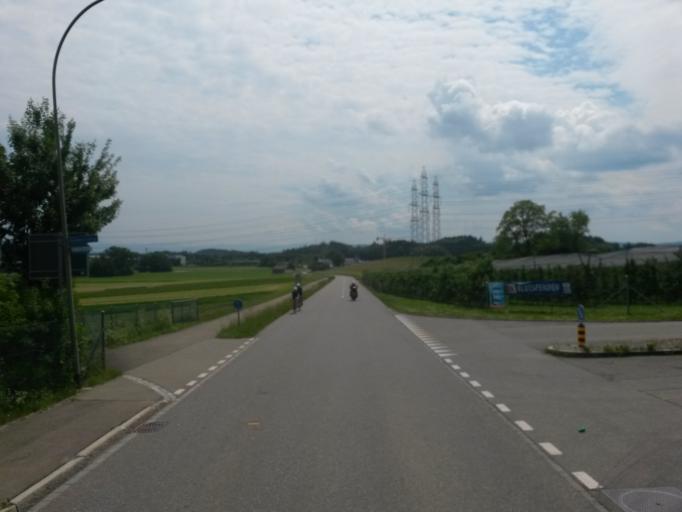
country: CH
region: Zurich
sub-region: Bezirk Pfaeffikon
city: Tagelswangen
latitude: 47.4462
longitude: 8.6818
